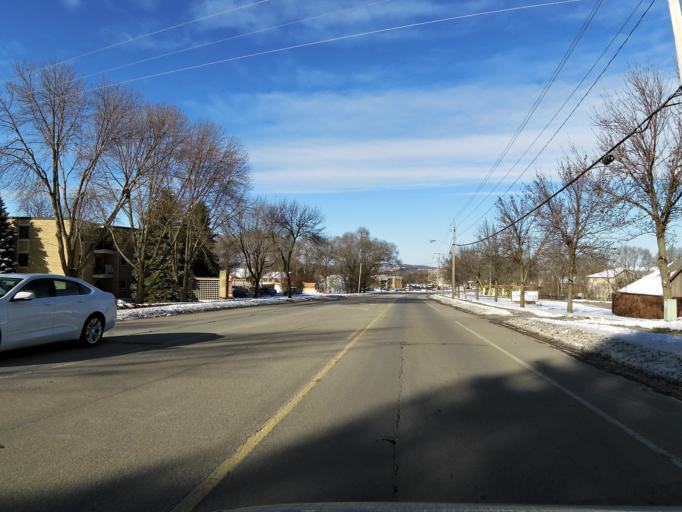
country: US
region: Minnesota
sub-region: Scott County
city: Shakopee
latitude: 44.7905
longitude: -93.5072
